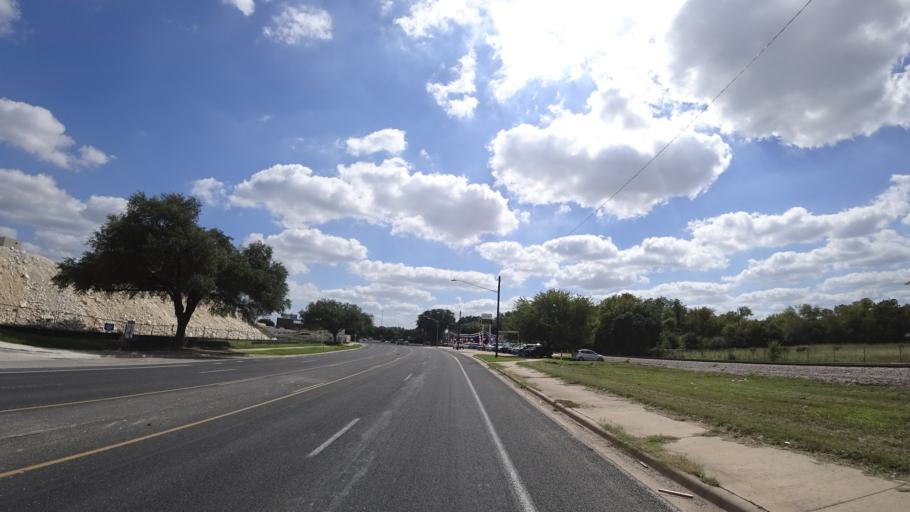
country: US
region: Texas
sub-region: Travis County
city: Austin
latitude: 30.3253
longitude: -97.7160
